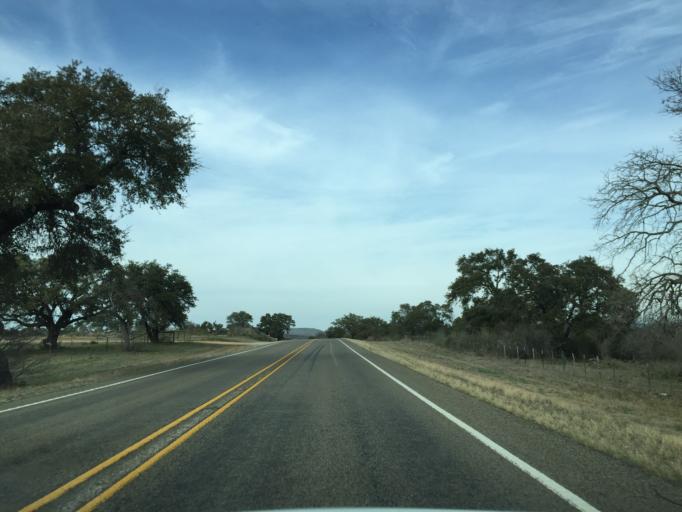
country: US
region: Texas
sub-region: Llano County
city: Llano
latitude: 30.5175
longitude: -98.7073
